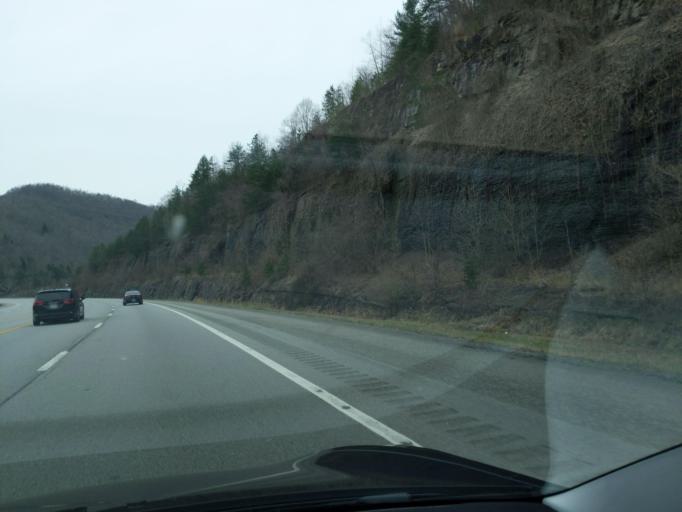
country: US
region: Kentucky
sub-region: Bell County
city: Pineville
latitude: 36.7774
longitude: -83.7372
